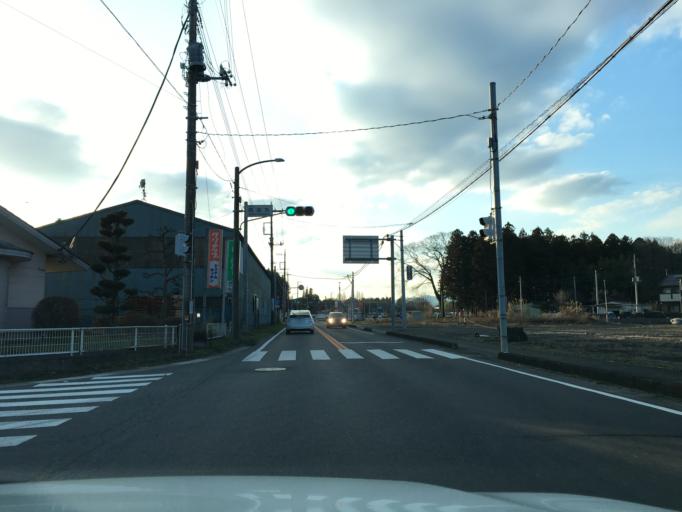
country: JP
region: Tochigi
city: Otawara
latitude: 36.8604
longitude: 140.0903
